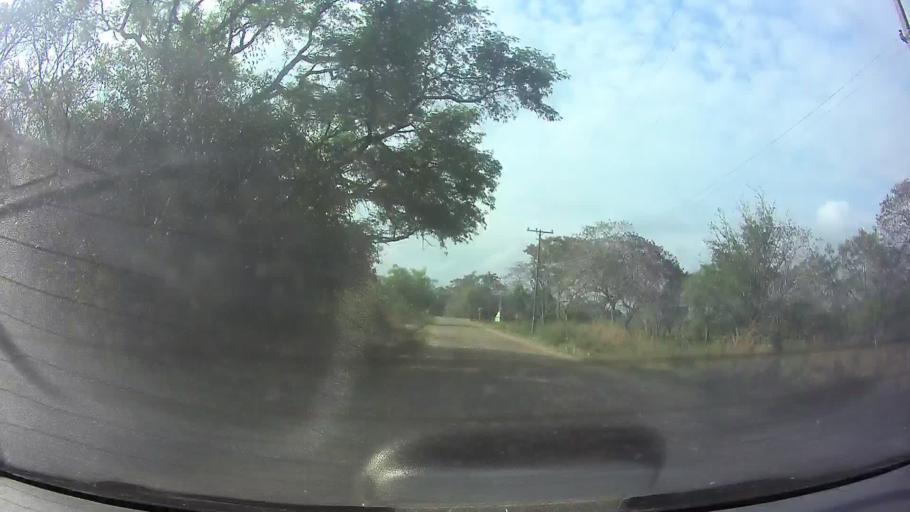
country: PY
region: Cordillera
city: Arroyos y Esteros
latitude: -24.9927
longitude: -57.1927
